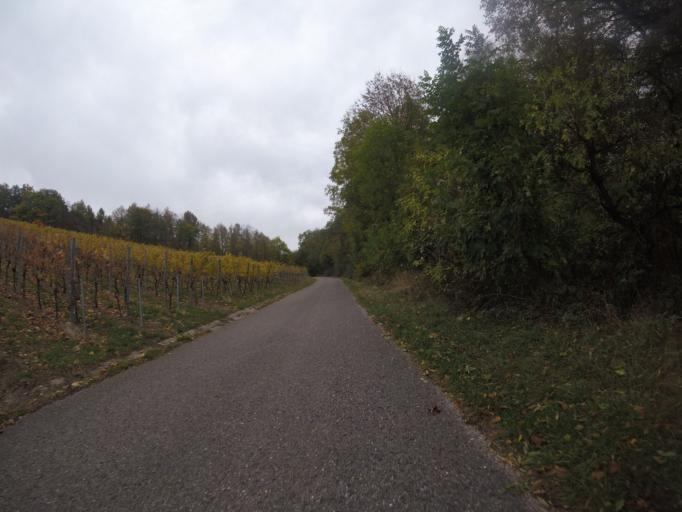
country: DE
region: Baden-Wuerttemberg
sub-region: Regierungsbezirk Stuttgart
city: Grossbottwar
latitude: 48.9930
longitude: 9.3200
